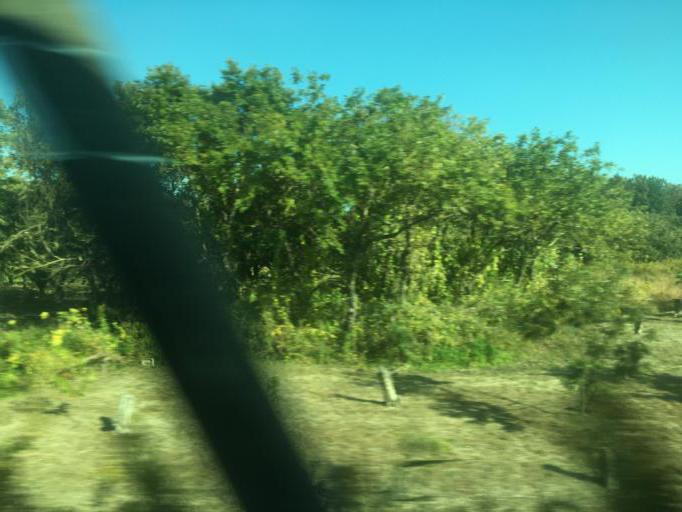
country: JP
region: Ibaraki
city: Tomobe
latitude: 36.2834
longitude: 140.2779
